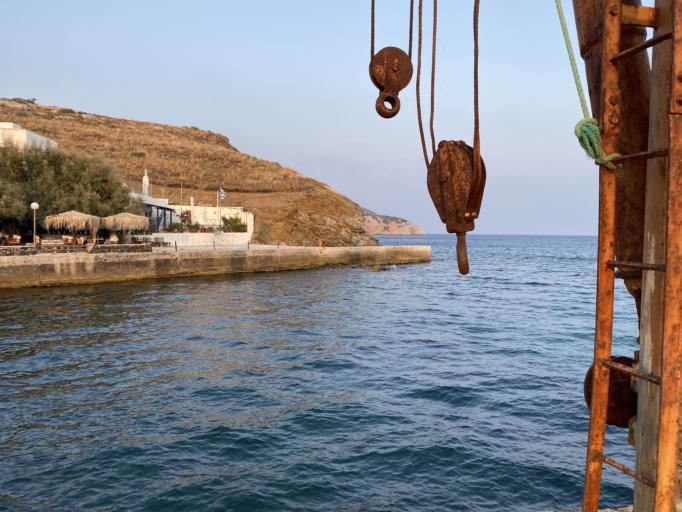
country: GR
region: South Aegean
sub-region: Nomos Kykladon
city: Filotion
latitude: 37.0779
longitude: 25.5875
